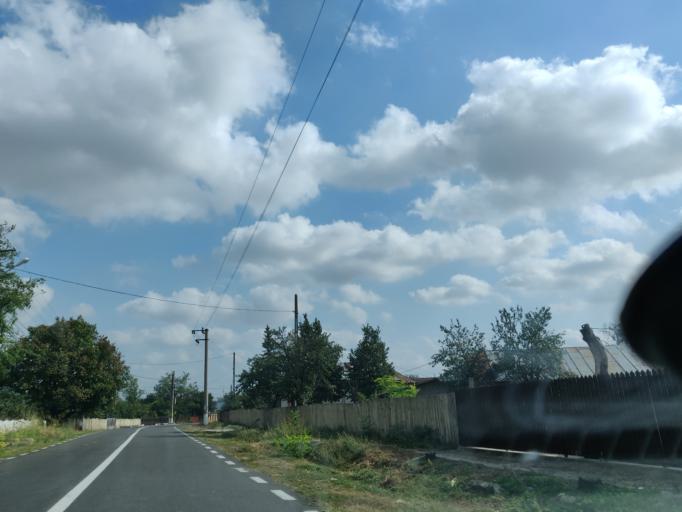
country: RO
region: Vrancea
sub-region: Comuna Ciorasti
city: Ciorasti
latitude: 45.4289
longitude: 27.2956
